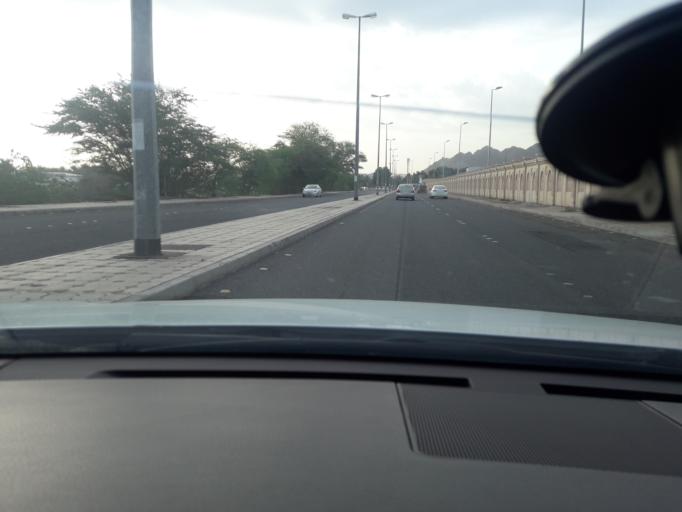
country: SA
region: Al Madinah al Munawwarah
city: Sultanah
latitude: 24.4784
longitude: 39.5679
